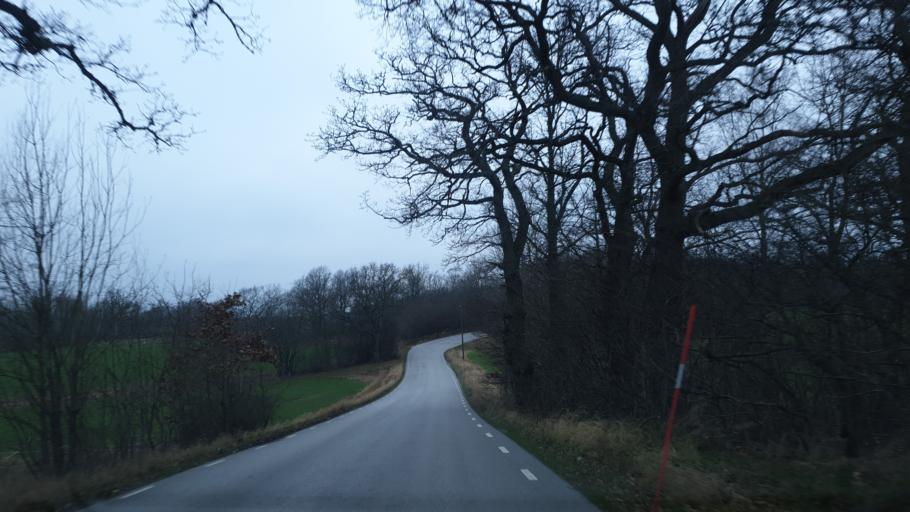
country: SE
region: Blekinge
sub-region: Karlskrona Kommun
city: Rodeby
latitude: 56.2013
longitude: 15.6868
